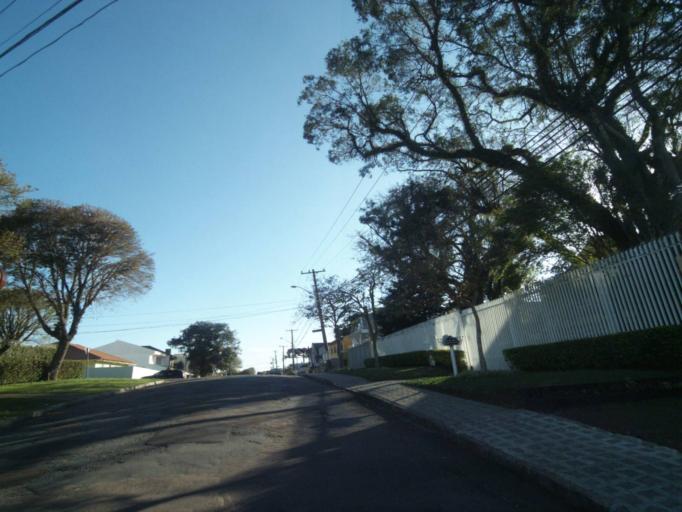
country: BR
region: Parana
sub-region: Curitiba
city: Curitiba
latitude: -25.3890
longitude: -49.2550
